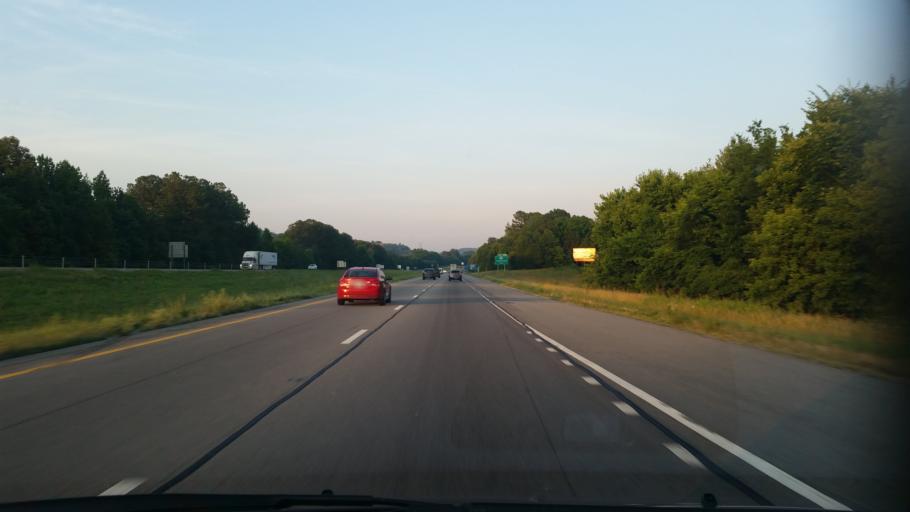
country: US
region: Tennessee
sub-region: Putnam County
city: Cookeville
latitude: 36.1348
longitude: -85.4723
